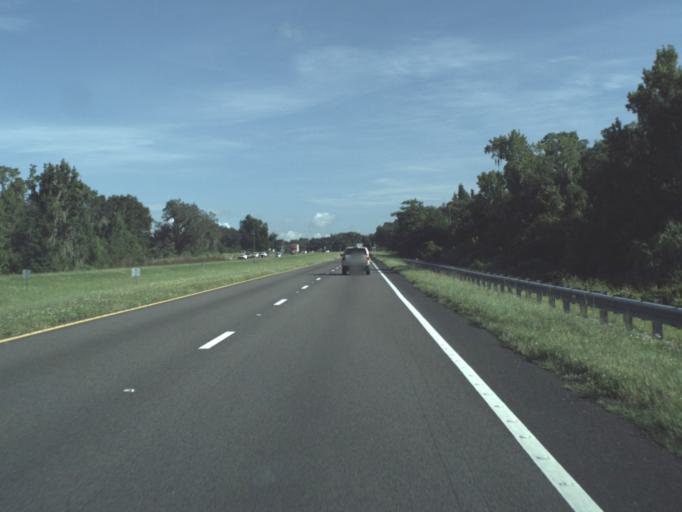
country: US
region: Florida
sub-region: Hardee County
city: Bowling Green
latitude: 27.6212
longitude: -81.8252
